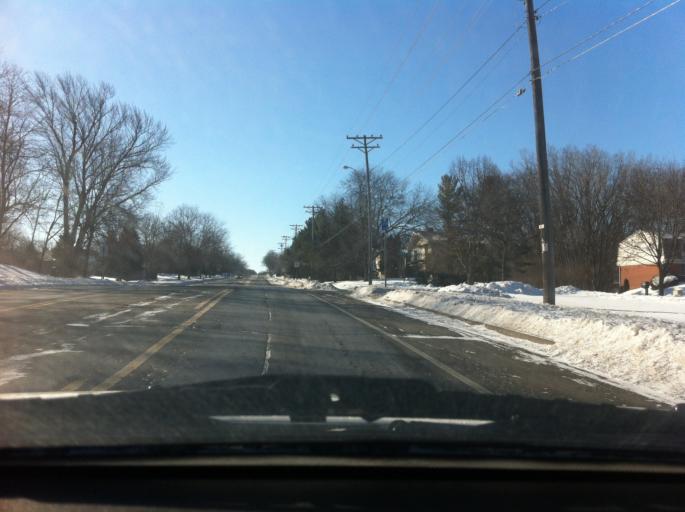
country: US
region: Wisconsin
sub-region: Dane County
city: Middleton
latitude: 43.0884
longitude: -89.5021
